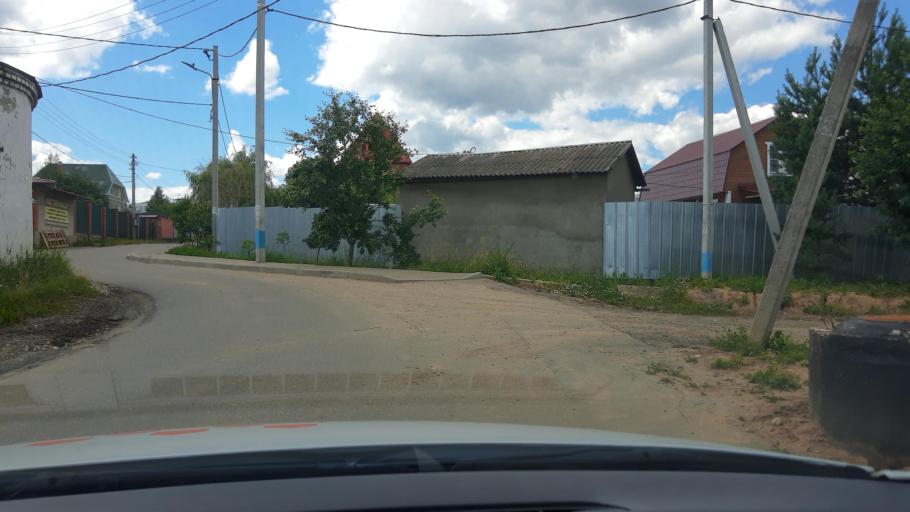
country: RU
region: Moskovskaya
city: Poselok Mar'ino
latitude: 55.5484
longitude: 37.3319
